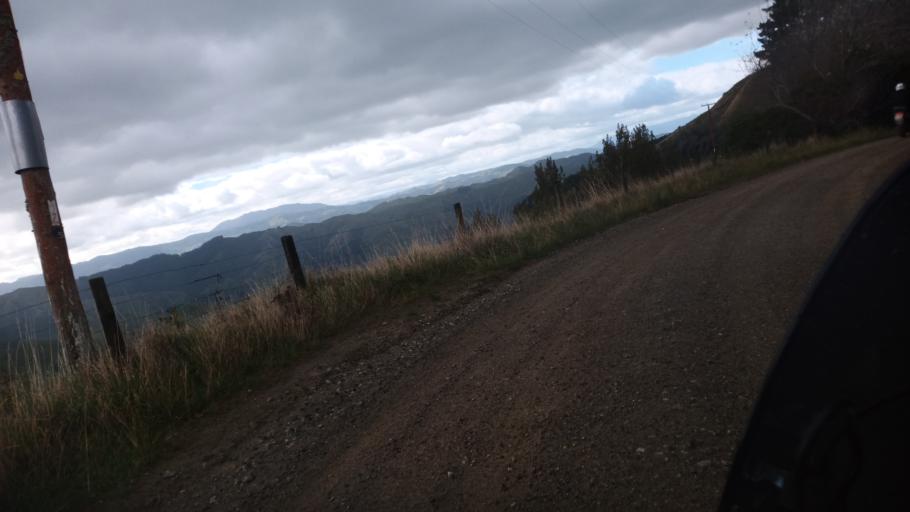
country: NZ
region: Gisborne
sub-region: Gisborne District
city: Gisborne
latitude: -38.4771
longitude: 177.6115
